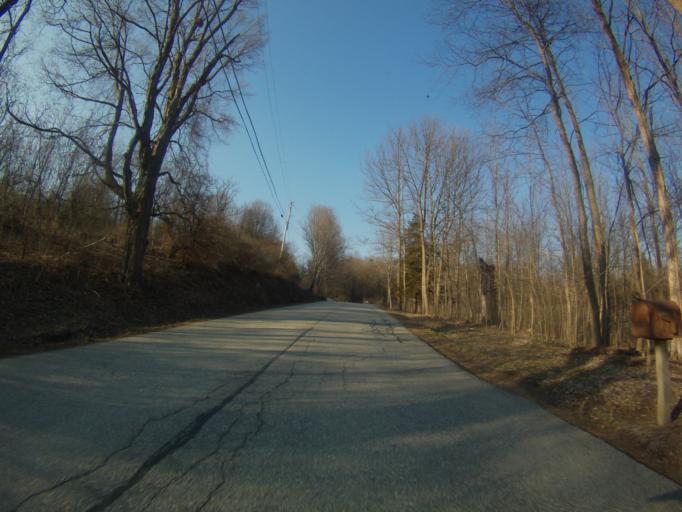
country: US
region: Vermont
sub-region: Addison County
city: Middlebury (village)
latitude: 44.0310
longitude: -73.1455
